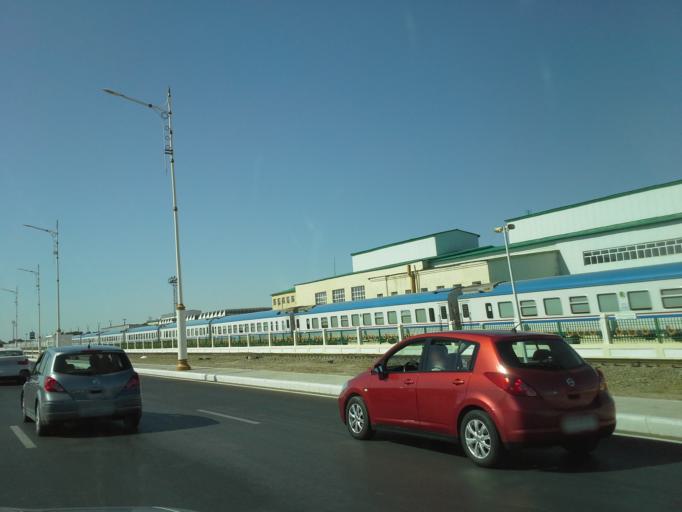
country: TM
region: Ahal
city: Ashgabat
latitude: 37.9347
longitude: 58.4120
